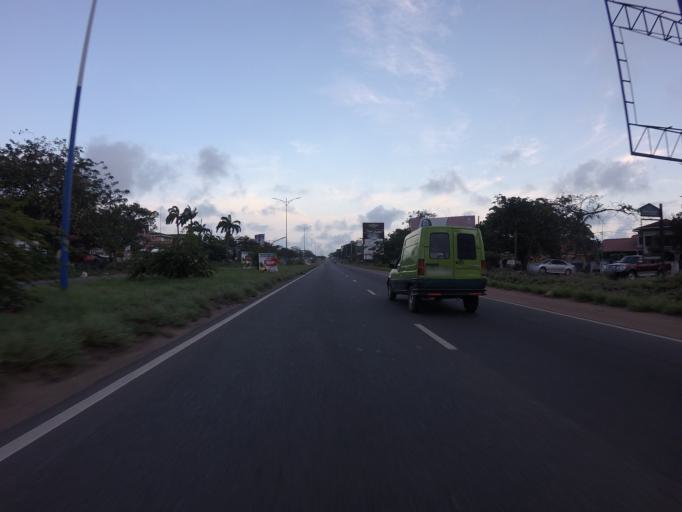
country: GH
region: Greater Accra
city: Accra
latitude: 5.5641
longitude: -0.1759
